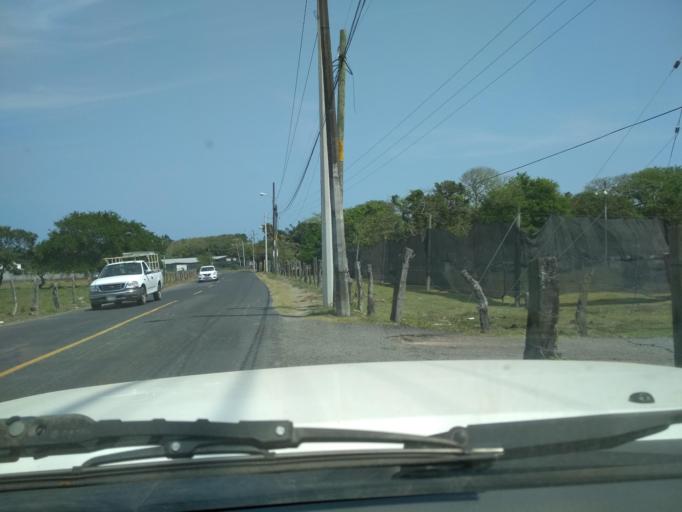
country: MX
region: Veracruz
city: Boca del Rio
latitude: 19.0948
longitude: -96.1193
